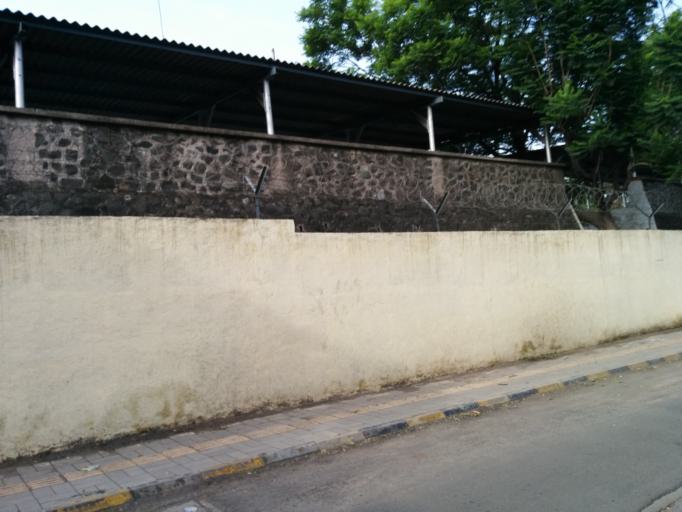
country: IN
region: Maharashtra
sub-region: Pune Division
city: Pune
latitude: 18.5063
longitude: 73.9097
